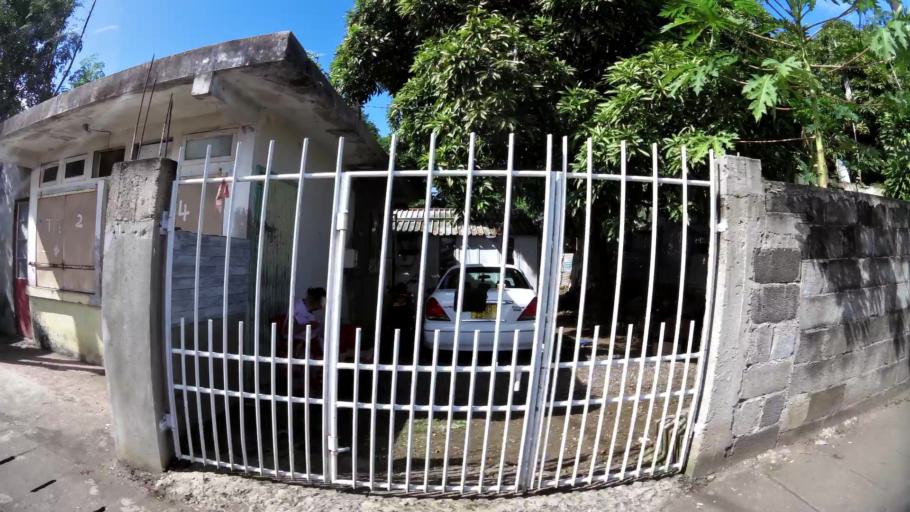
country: MU
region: Grand Port
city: Plaine Magnien
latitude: -20.4346
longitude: 57.6591
